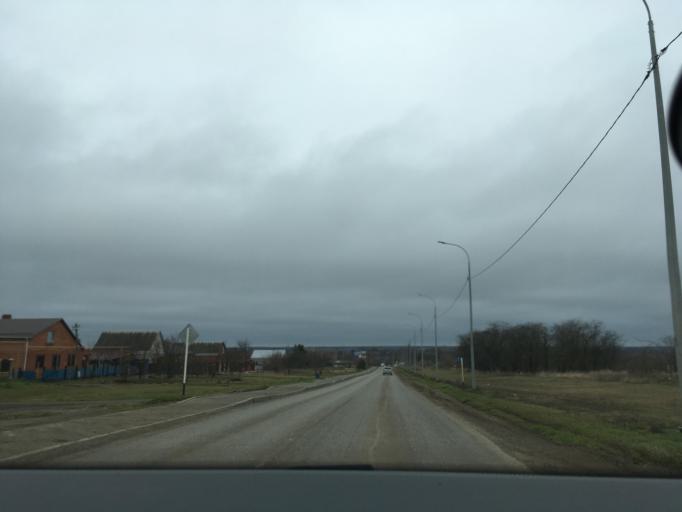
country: RU
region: Krasnodarskiy
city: Kushchevskaya
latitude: 46.5829
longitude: 39.6400
